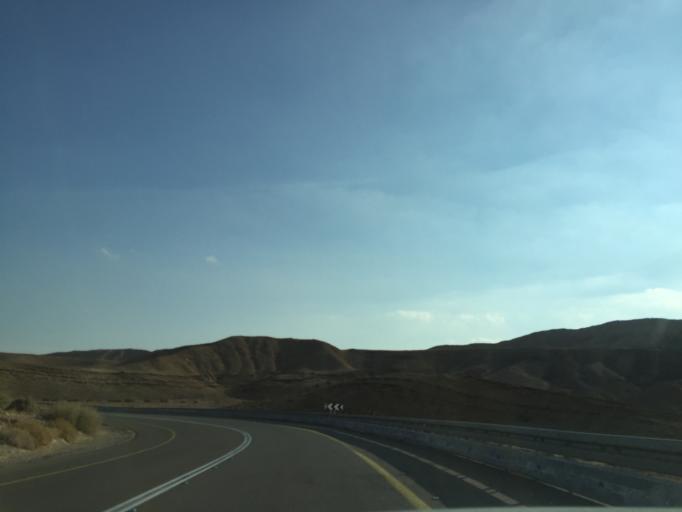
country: IL
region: Southern District
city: `En Boqeq
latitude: 31.1759
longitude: 35.2973
